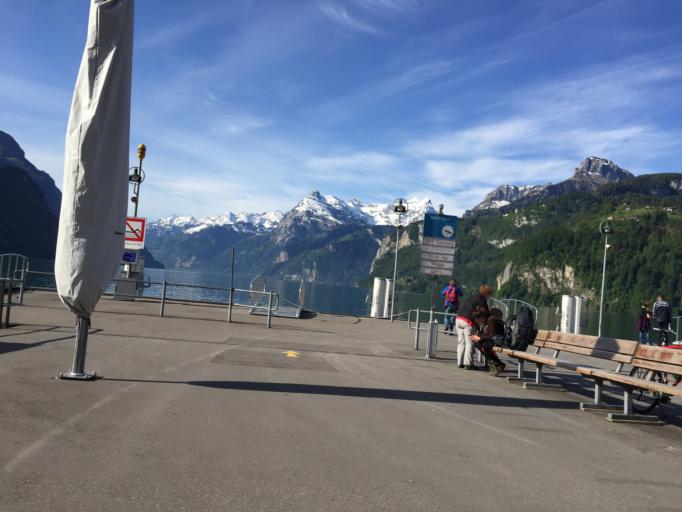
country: CH
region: Schwyz
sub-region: Bezirk Schwyz
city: Ingenbohl
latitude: 46.9935
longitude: 8.6054
